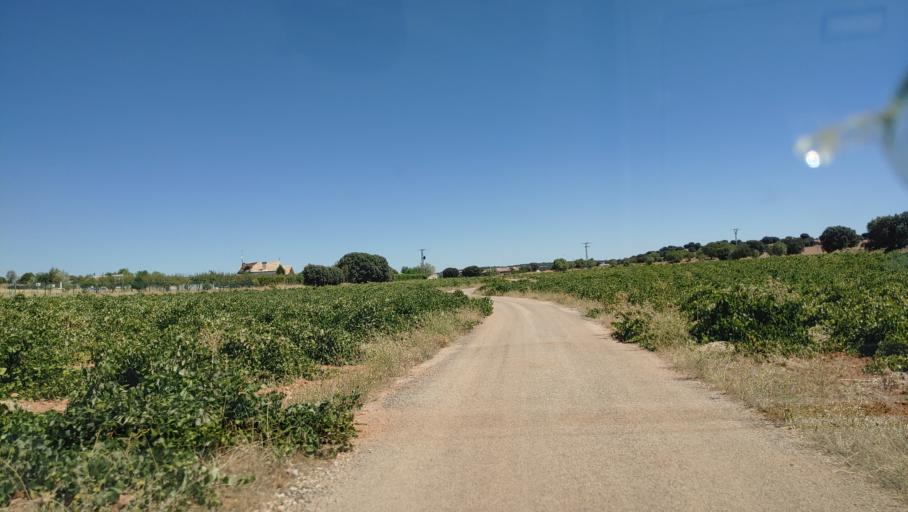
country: ES
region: Castille-La Mancha
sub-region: Provincia de Albacete
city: Ossa de Montiel
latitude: 38.9331
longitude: -2.7638
